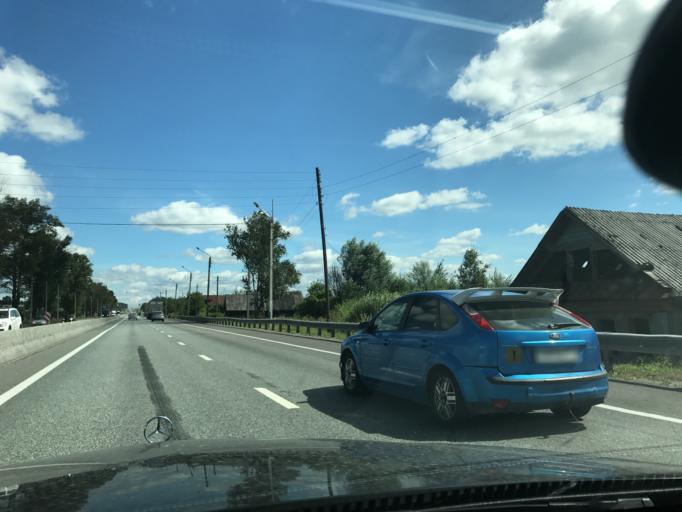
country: RU
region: Nizjnij Novgorod
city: Novosmolinskiy
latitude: 56.2769
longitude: 42.9868
